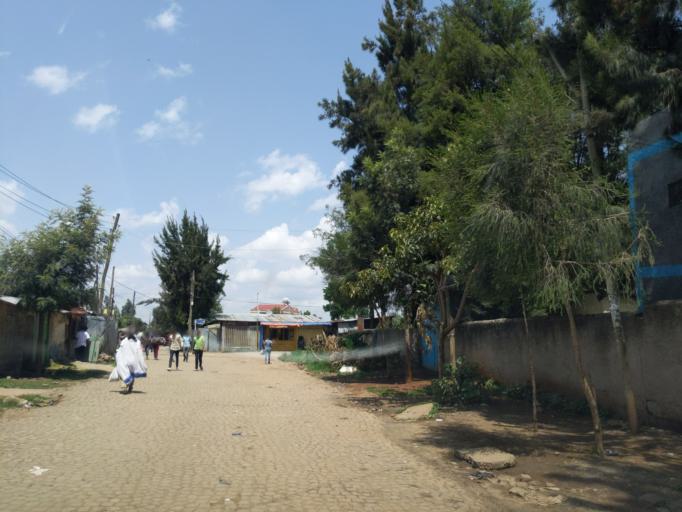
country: ET
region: Adis Abeba
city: Addis Ababa
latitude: 8.9460
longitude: 38.7548
